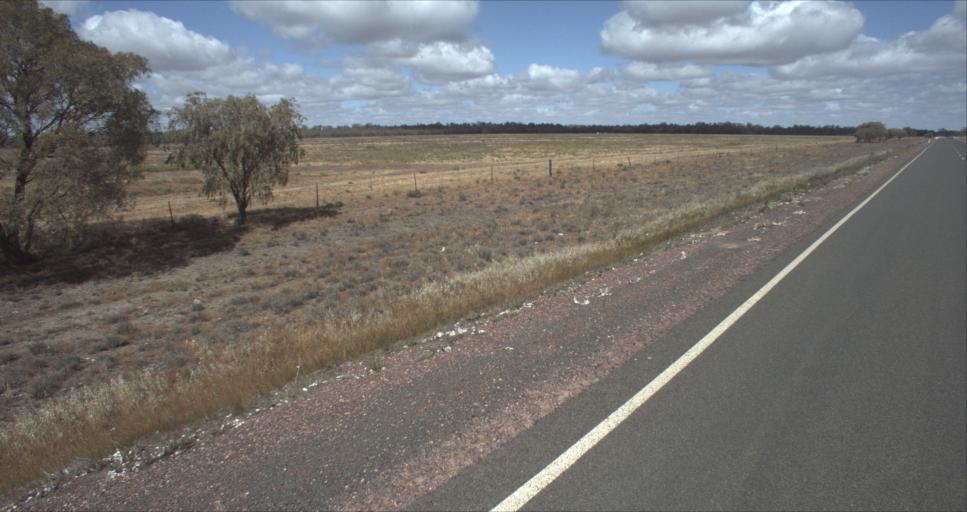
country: AU
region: New South Wales
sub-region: Murrumbidgee Shire
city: Darlington Point
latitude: -34.5753
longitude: 146.0694
